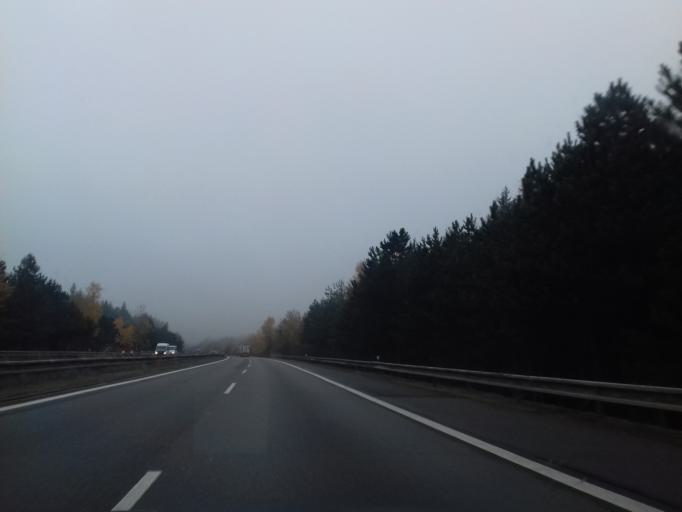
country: CZ
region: Vysocina
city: Vilemov
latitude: 49.5236
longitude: 15.3779
